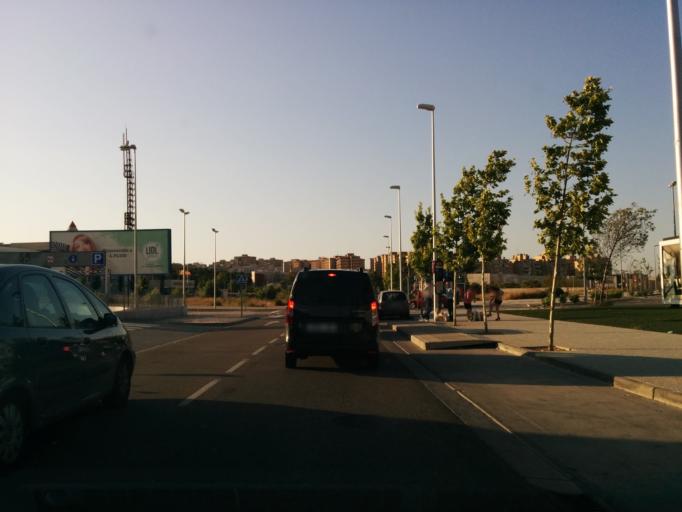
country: ES
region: Aragon
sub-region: Provincia de Zaragoza
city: Zaragoza
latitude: 41.6185
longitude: -0.8762
